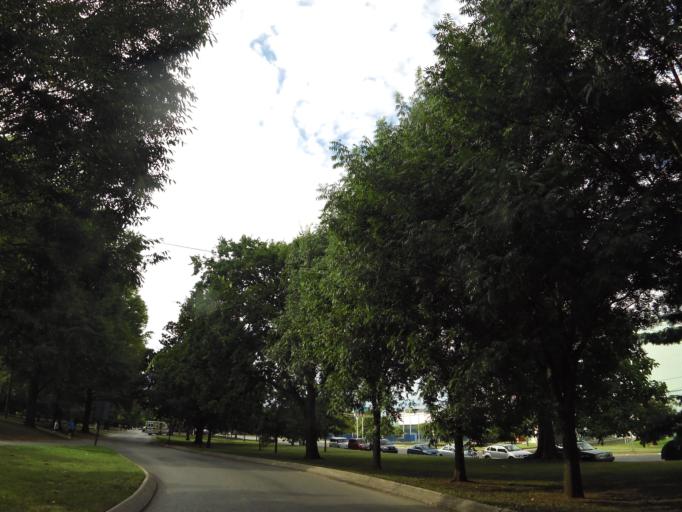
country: US
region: Tennessee
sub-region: Davidson County
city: Nashville
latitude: 36.1491
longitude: -86.8102
